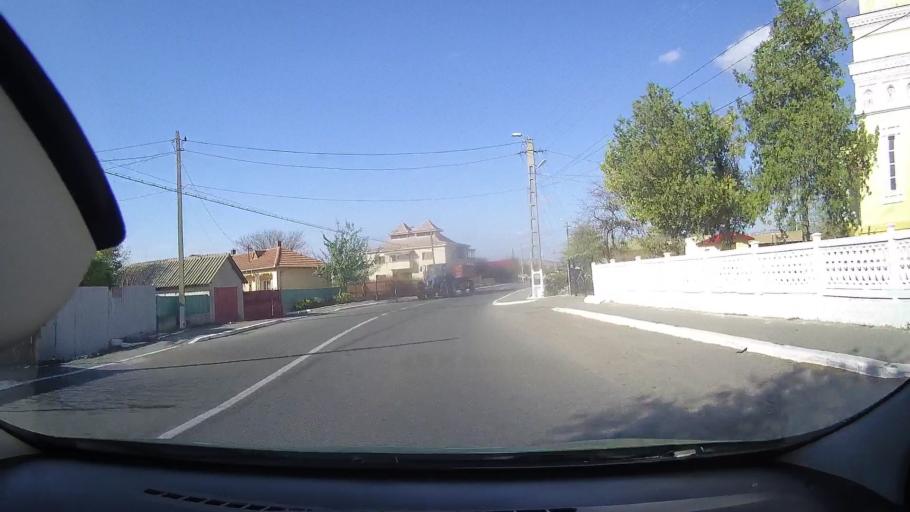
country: RO
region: Tulcea
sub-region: Comuna Ceamurlia de Jos
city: Ceamurlia de Jos
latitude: 44.7431
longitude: 28.7232
